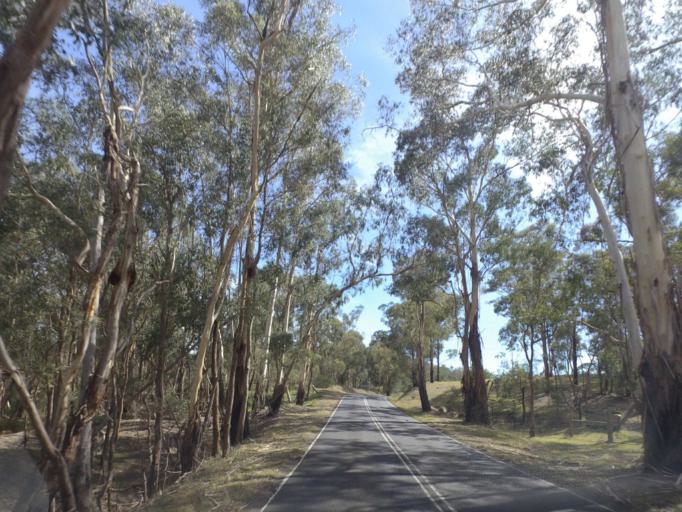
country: AU
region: Victoria
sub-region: Nillumbik
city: Saint Andrews
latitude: -37.6078
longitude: 145.2520
